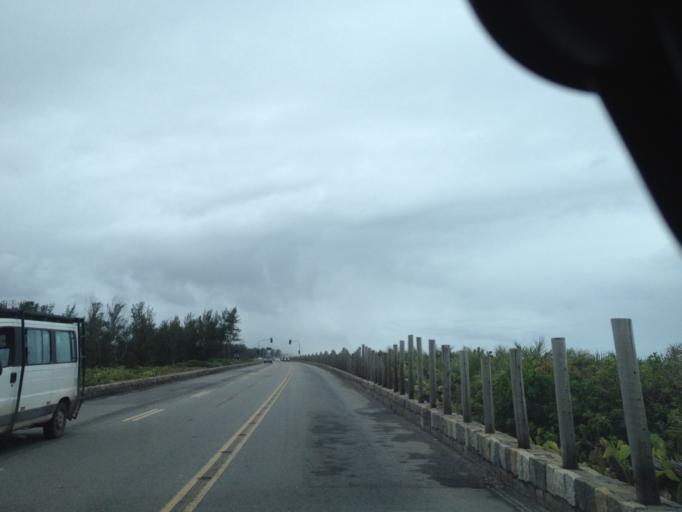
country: BR
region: Rio de Janeiro
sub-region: Nilopolis
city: Nilopolis
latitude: -23.0190
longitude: -43.4302
